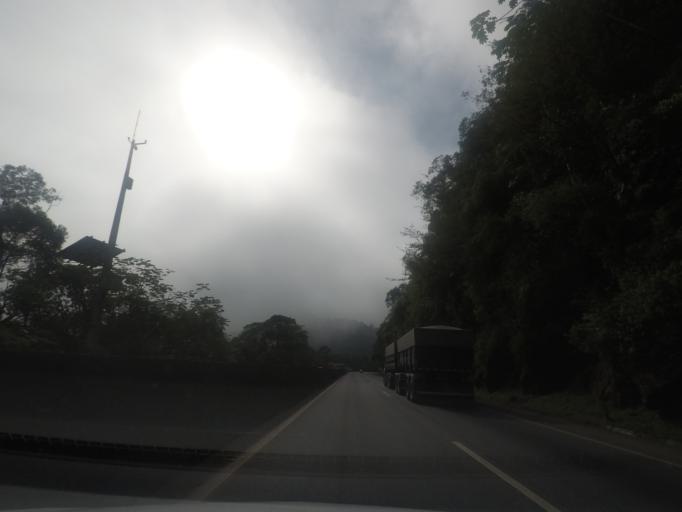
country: BR
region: Parana
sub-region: Antonina
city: Antonina
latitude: -25.5923
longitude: -48.8805
